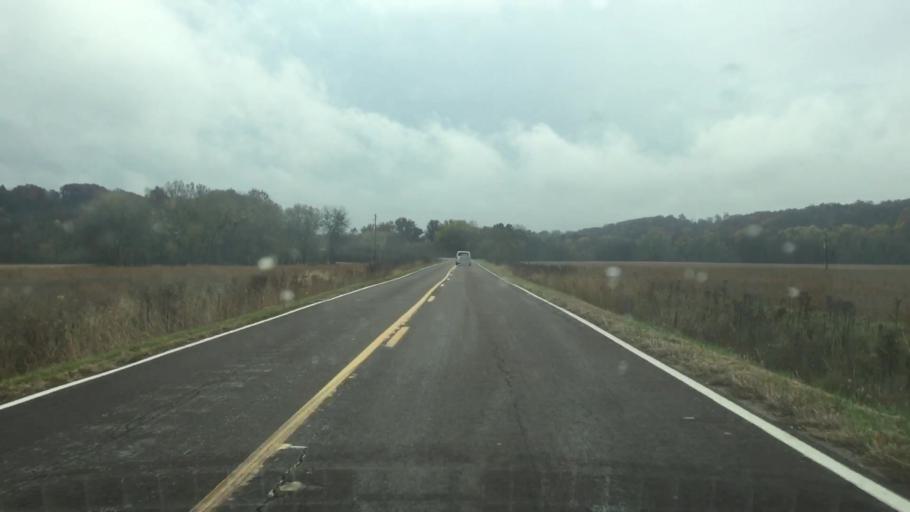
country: US
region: Missouri
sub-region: Callaway County
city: Fulton
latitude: 38.7842
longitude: -91.8546
